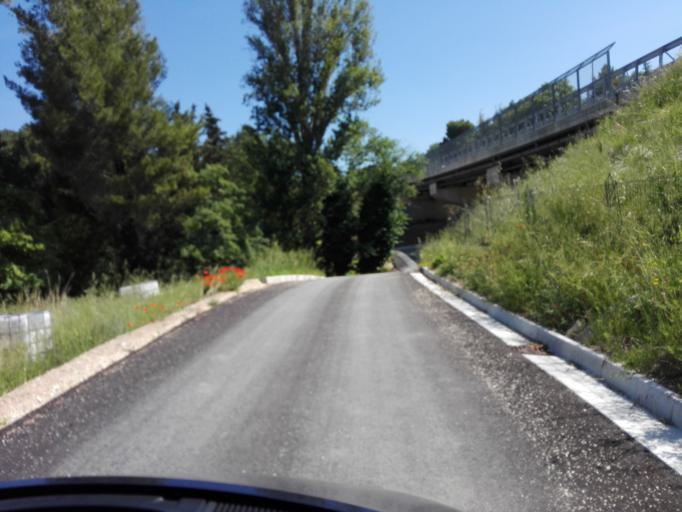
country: IT
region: Umbria
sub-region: Provincia di Perugia
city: Foligno
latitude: 42.9566
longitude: 12.7343
